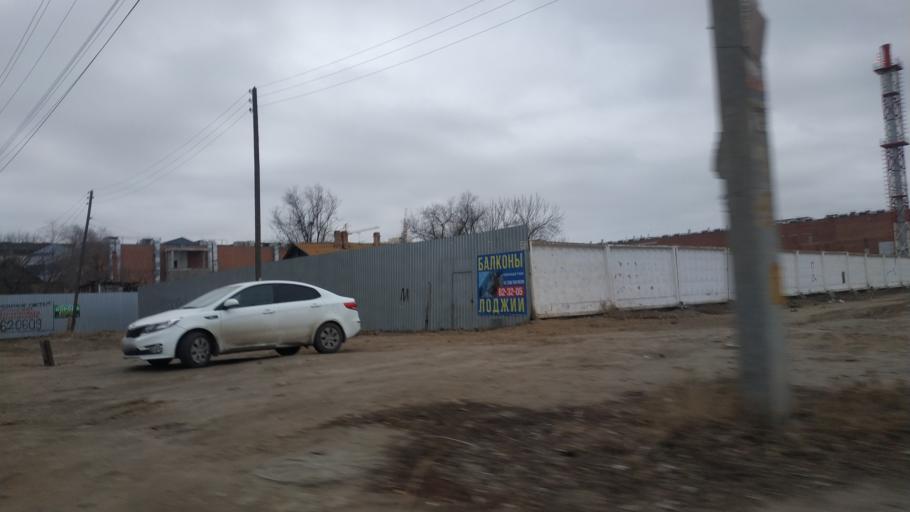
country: RU
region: Astrakhan
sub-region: Gorod Astrakhan'
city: Astrakhan'
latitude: 46.3369
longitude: 48.0258
